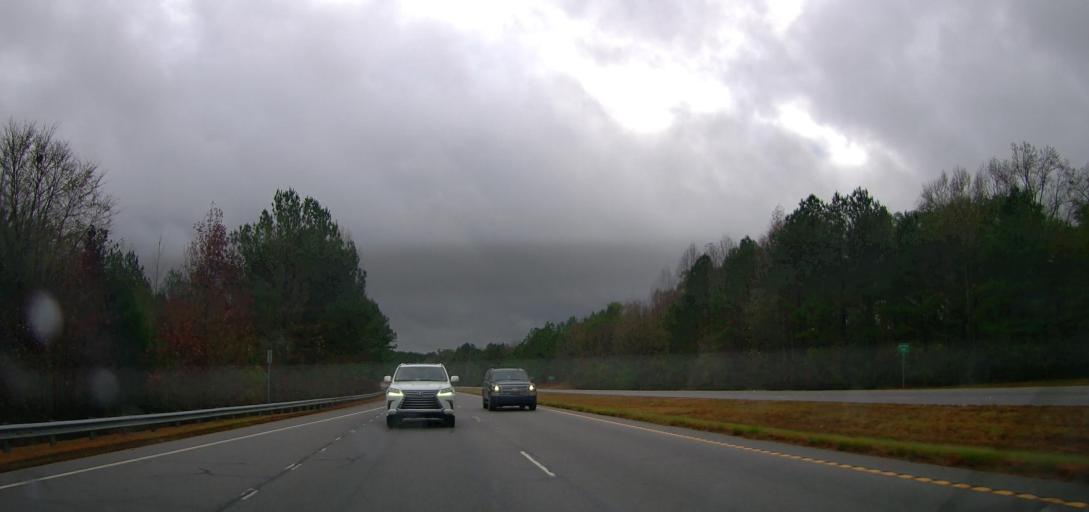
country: US
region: Georgia
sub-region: Oconee County
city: Watkinsville
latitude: 33.8659
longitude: -83.4237
